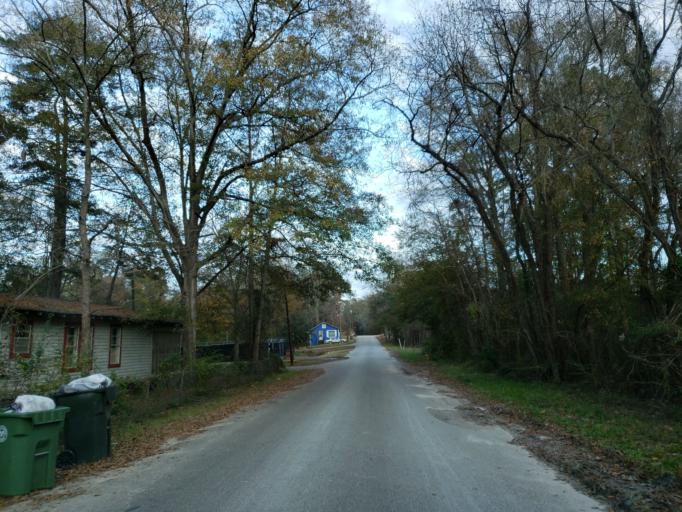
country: US
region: Mississippi
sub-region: Forrest County
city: Hattiesburg
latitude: 31.3029
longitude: -89.3189
